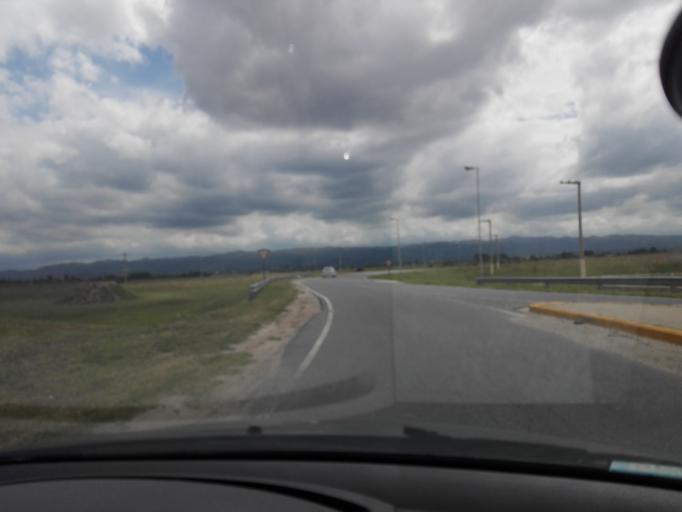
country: AR
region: Cordoba
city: Alta Gracia
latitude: -31.6361
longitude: -64.4036
